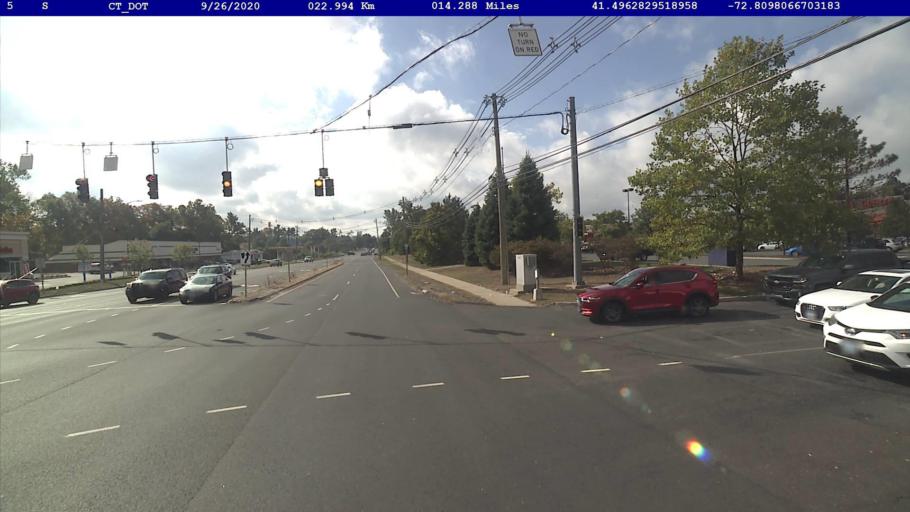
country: US
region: Connecticut
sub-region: New Haven County
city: Wallingford
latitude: 41.4963
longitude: -72.8098
